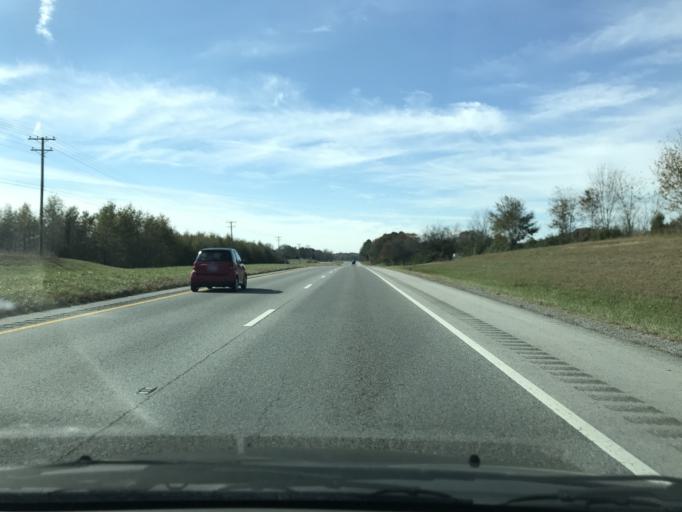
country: US
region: Tennessee
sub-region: Coffee County
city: Manchester
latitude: 35.4081
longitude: -86.1250
